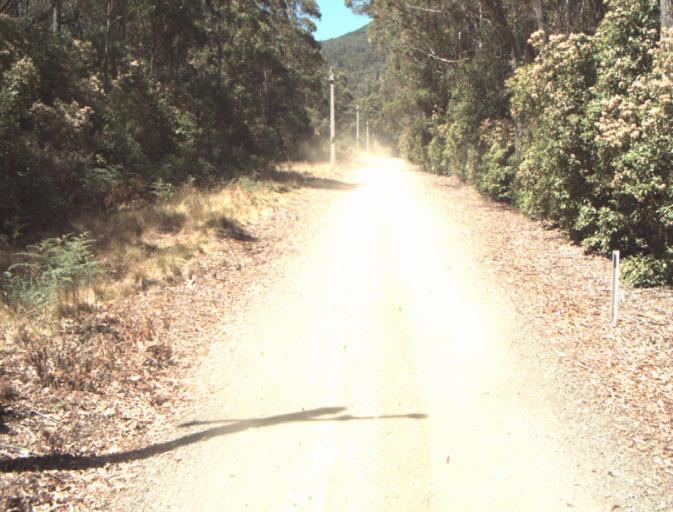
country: AU
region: Tasmania
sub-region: Dorset
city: Scottsdale
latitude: -41.3546
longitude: 147.3903
